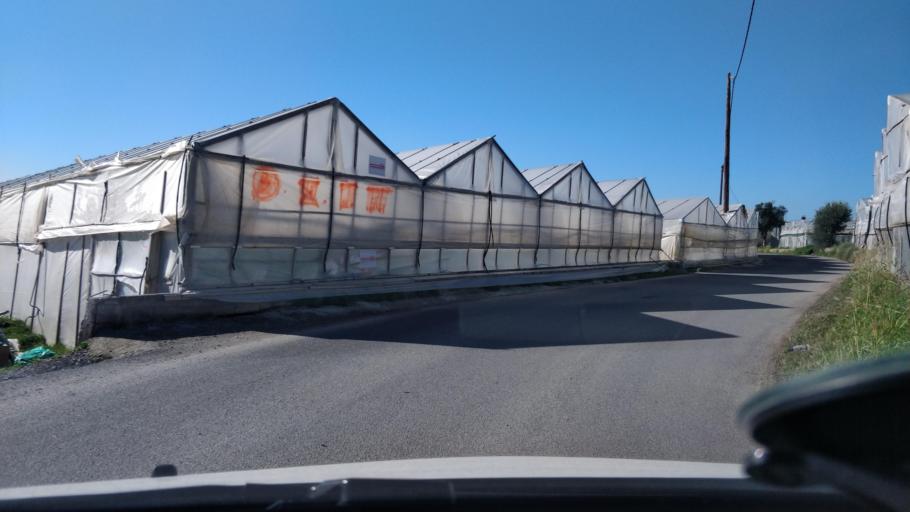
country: GR
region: Crete
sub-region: Nomos Lasithiou
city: Gra Liyia
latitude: 35.0184
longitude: 25.6774
